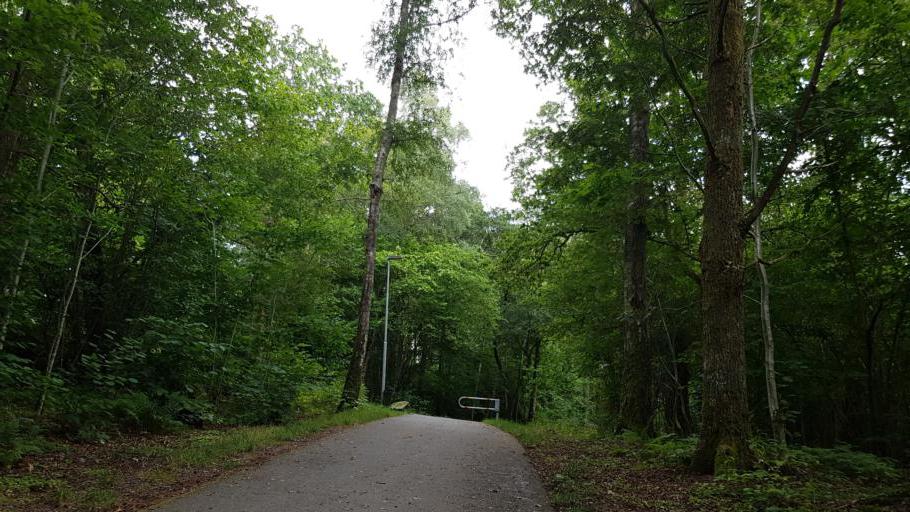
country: SE
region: Vaestra Goetaland
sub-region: Harryda Kommun
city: Molnlycke
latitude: 57.6658
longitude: 12.0972
